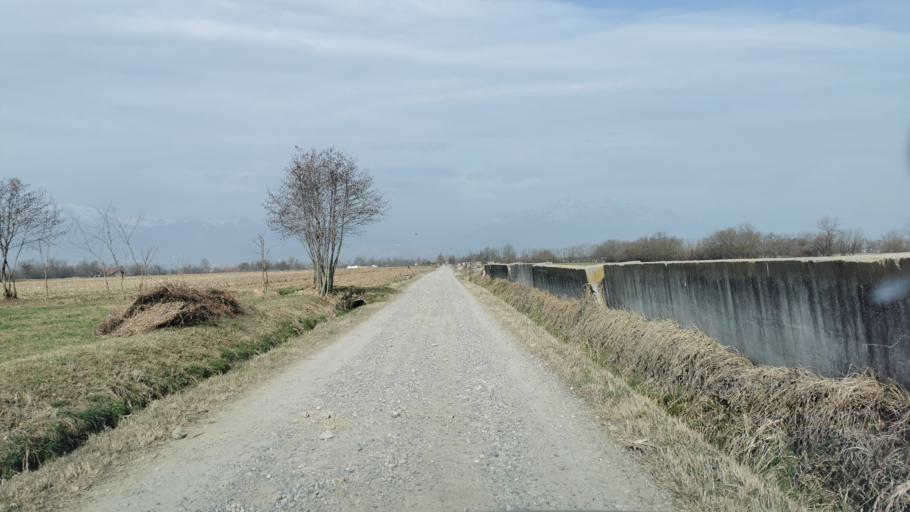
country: IT
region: Piedmont
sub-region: Provincia di Torino
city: Rivarossa
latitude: 45.2748
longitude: 7.7020
